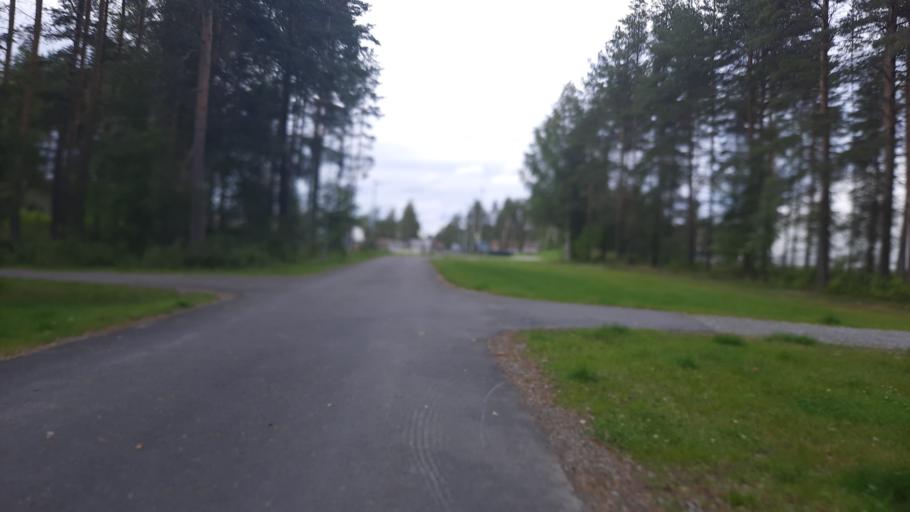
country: FI
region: North Karelia
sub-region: Joensuu
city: Joensuu
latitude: 62.6117
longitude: 29.8238
